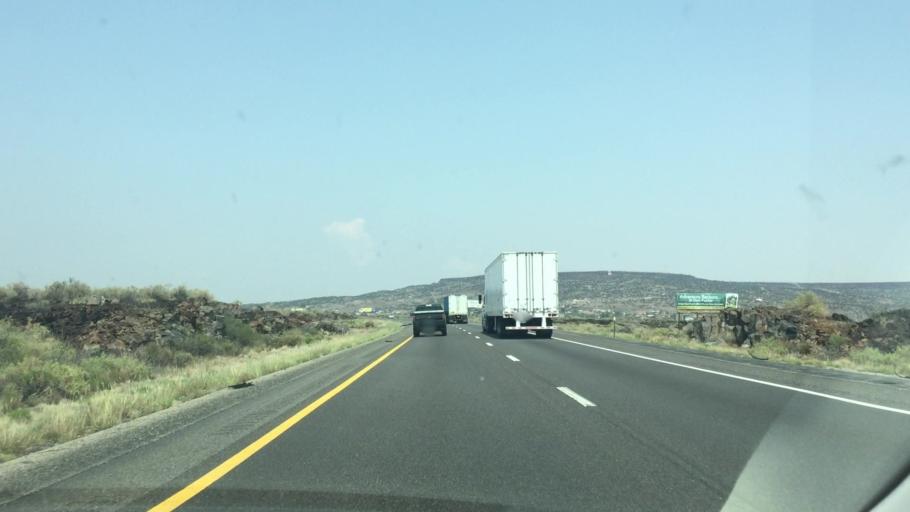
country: US
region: New Mexico
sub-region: Cibola County
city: Grants
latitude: 35.1386
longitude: -107.8460
